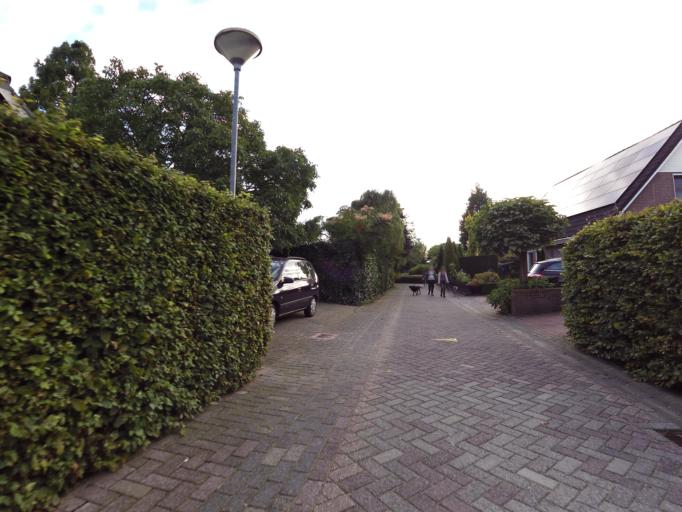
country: NL
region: Gelderland
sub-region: Gemeente Montferland
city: s-Heerenberg
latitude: 51.8790
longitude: 6.2683
